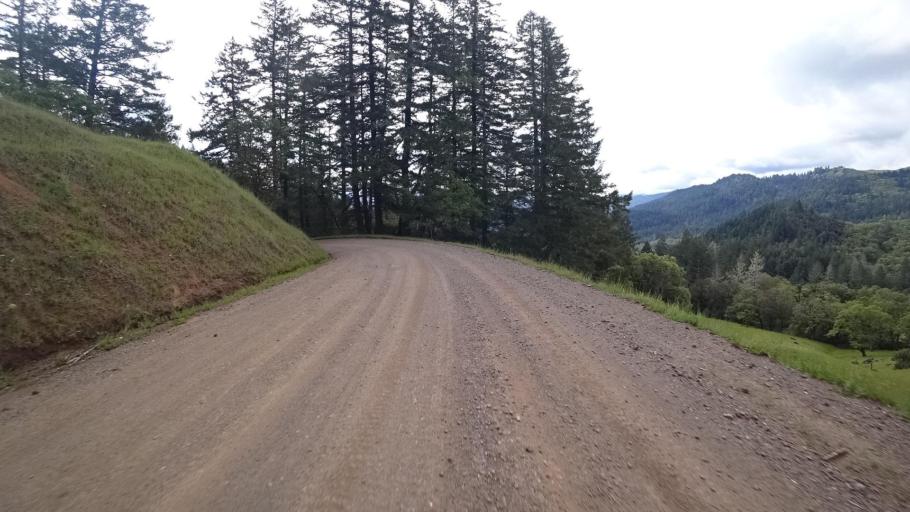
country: US
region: California
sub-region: Humboldt County
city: Redway
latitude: 40.2109
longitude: -123.6776
